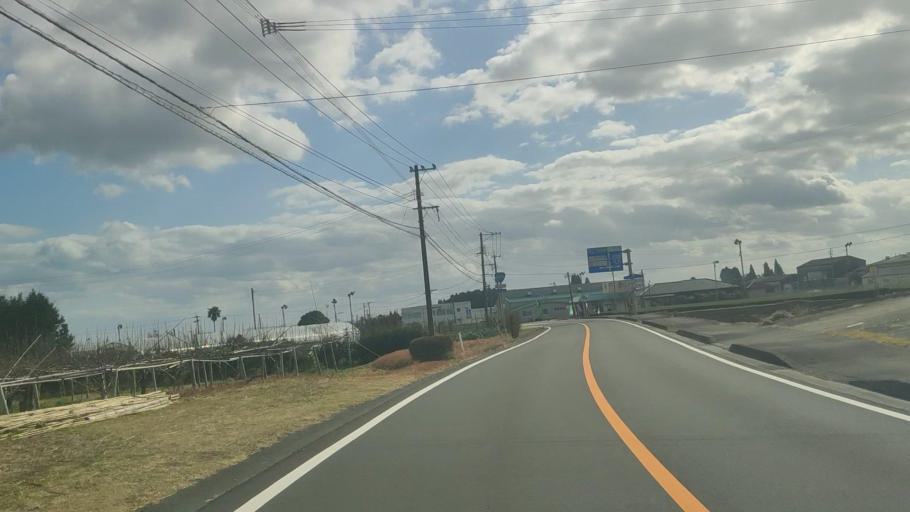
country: JP
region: Kagoshima
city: Kajiki
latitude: 31.8180
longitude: 130.7054
